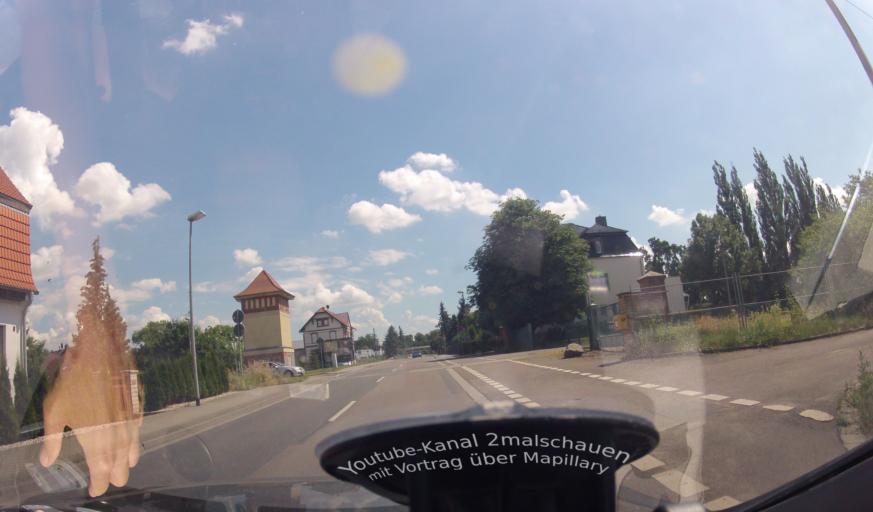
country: DE
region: Saxony
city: Torgau
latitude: 51.5678
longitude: 12.9963
